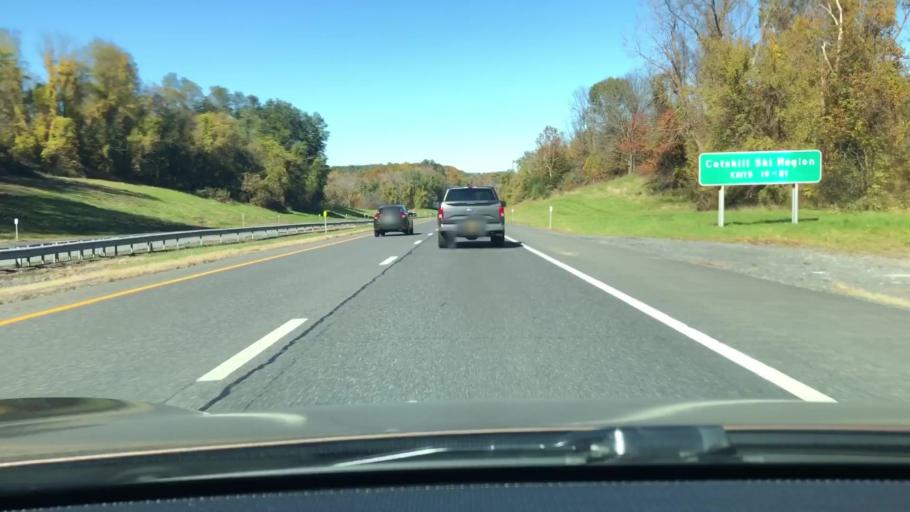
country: US
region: New York
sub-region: Ulster County
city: Rosendale Village
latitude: 41.8442
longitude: -74.0590
